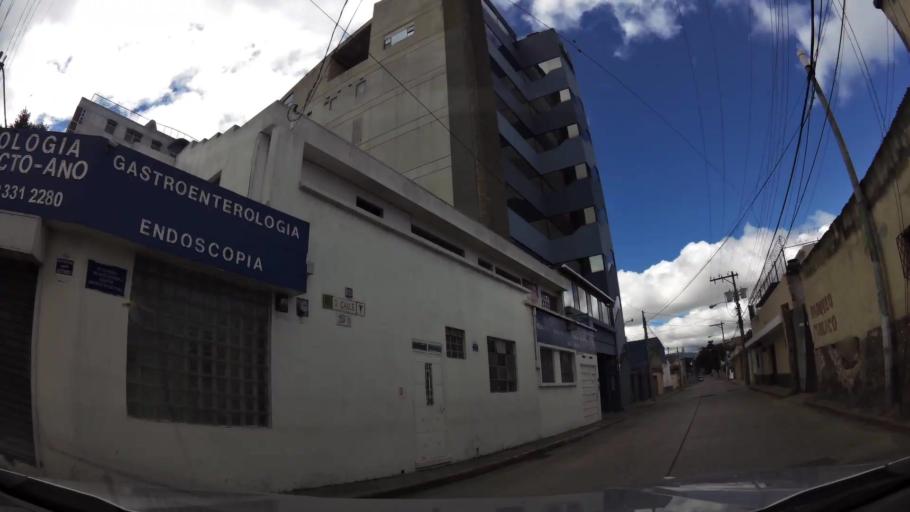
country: GT
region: Guatemala
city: Guatemala City
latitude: 14.6111
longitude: -90.5104
